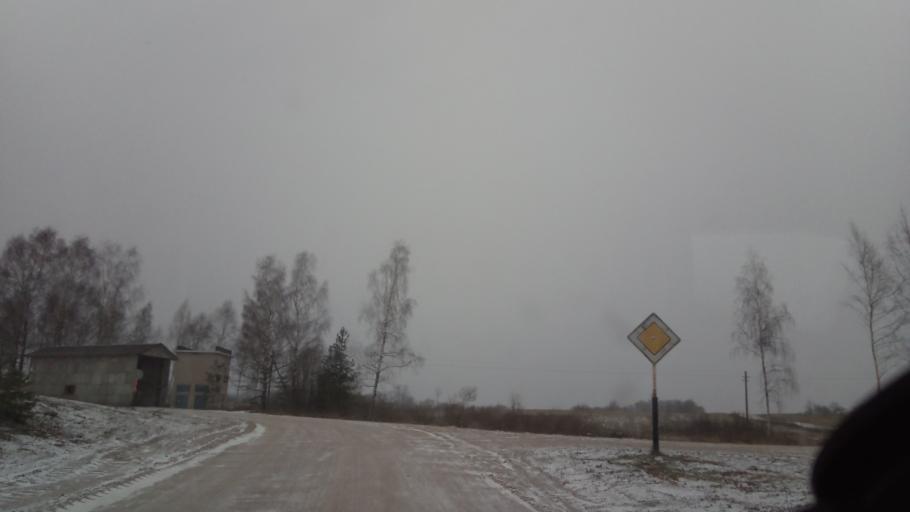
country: LT
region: Vilnius County
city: Ukmerge
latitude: 55.3321
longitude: 24.8812
